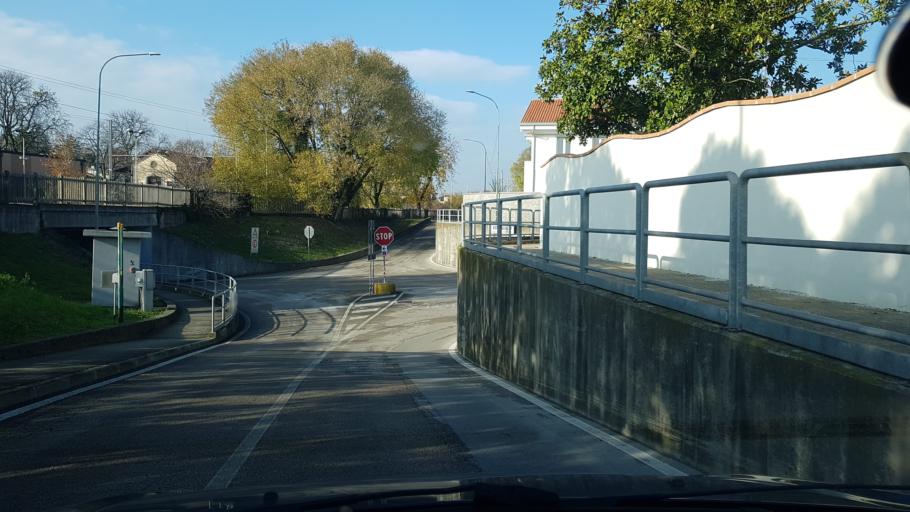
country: IT
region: Friuli Venezia Giulia
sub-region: Provincia di Gorizia
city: Ronchi dei Legionari
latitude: 45.8294
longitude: 13.5076
